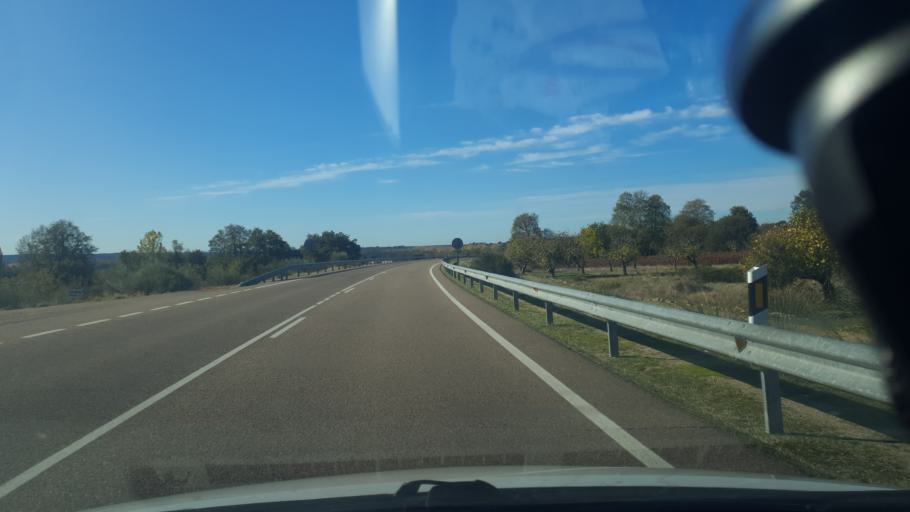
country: ES
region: Castille and Leon
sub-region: Provincia de Avila
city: Poyales del Hoyo
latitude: 40.1469
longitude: -5.1924
